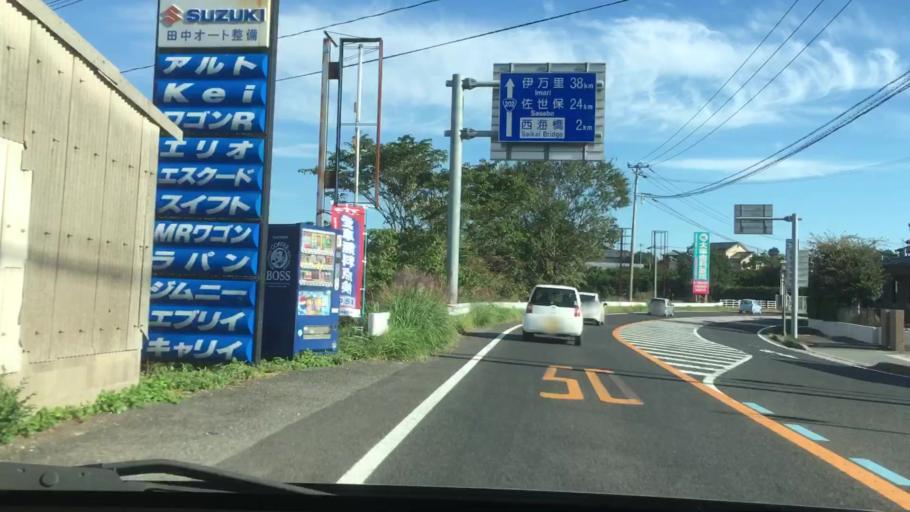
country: JP
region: Nagasaki
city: Sasebo
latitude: 33.0455
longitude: 129.7451
